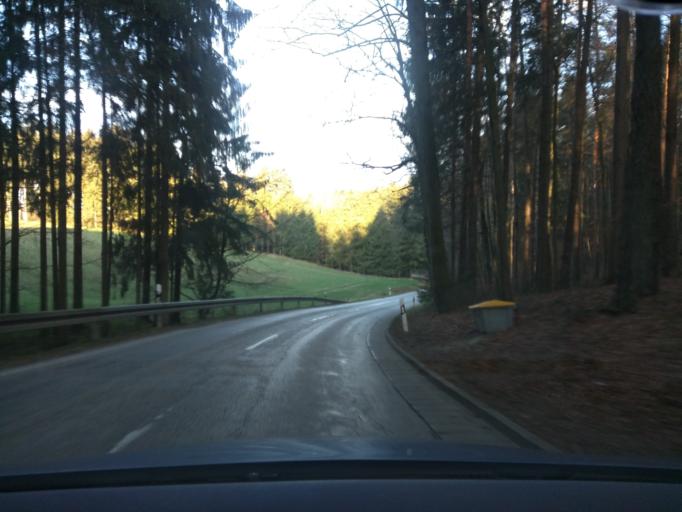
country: DE
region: Bavaria
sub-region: Upper Bavaria
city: Wolnzach
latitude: 48.5749
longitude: 11.6760
